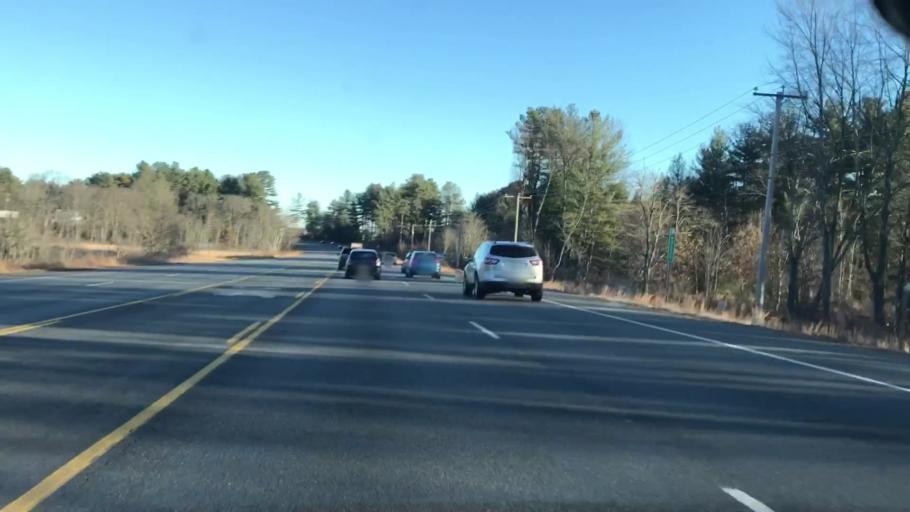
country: US
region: New Hampshire
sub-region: Hillsborough County
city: Hollis
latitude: 42.8035
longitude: -71.5600
